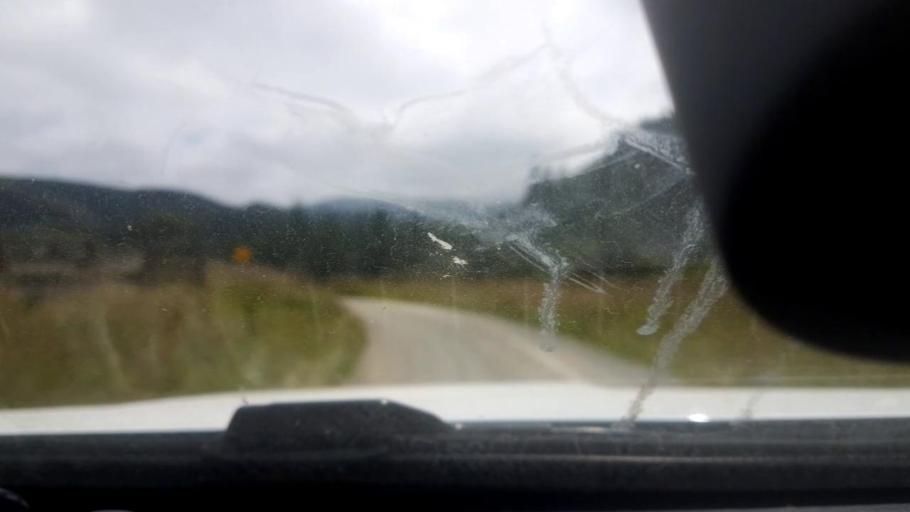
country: NZ
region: Canterbury
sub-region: Timaru District
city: Pleasant Point
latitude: -44.1394
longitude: 171.0835
